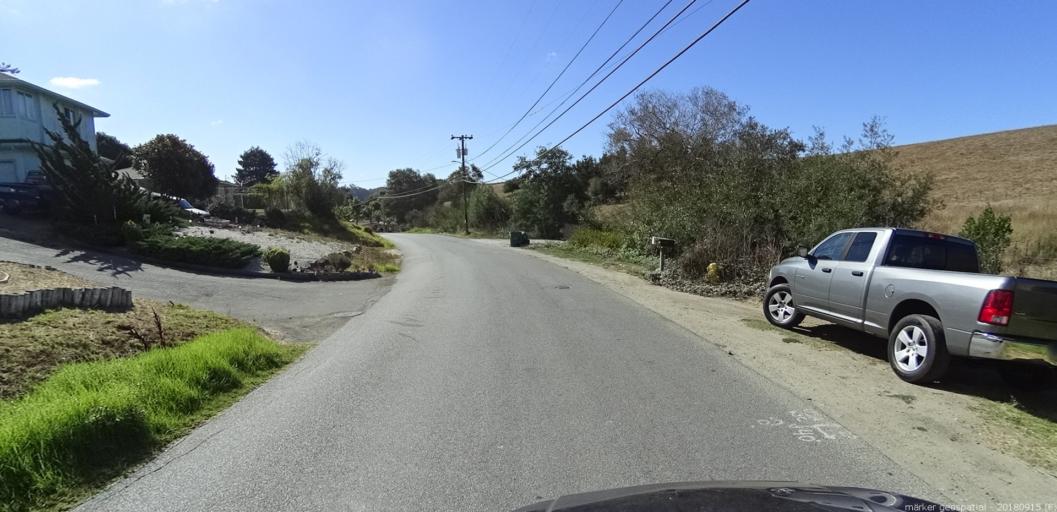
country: US
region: California
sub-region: Monterey County
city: Las Lomas
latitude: 36.8703
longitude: -121.7360
